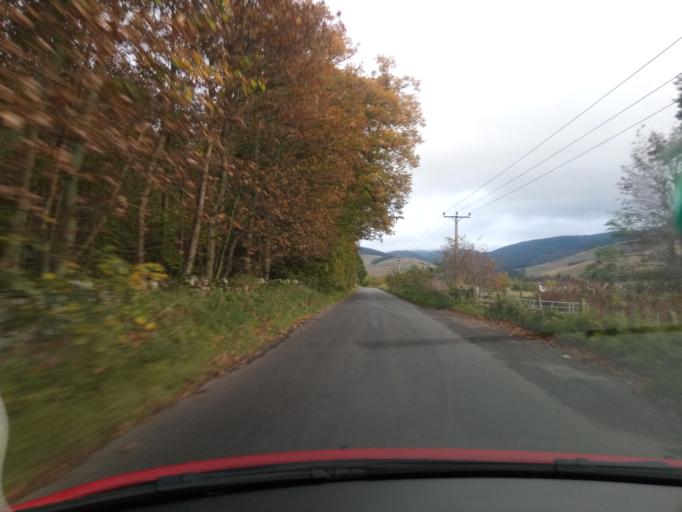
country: GB
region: Scotland
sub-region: The Scottish Borders
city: Innerleithen
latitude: 55.6311
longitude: -3.1044
